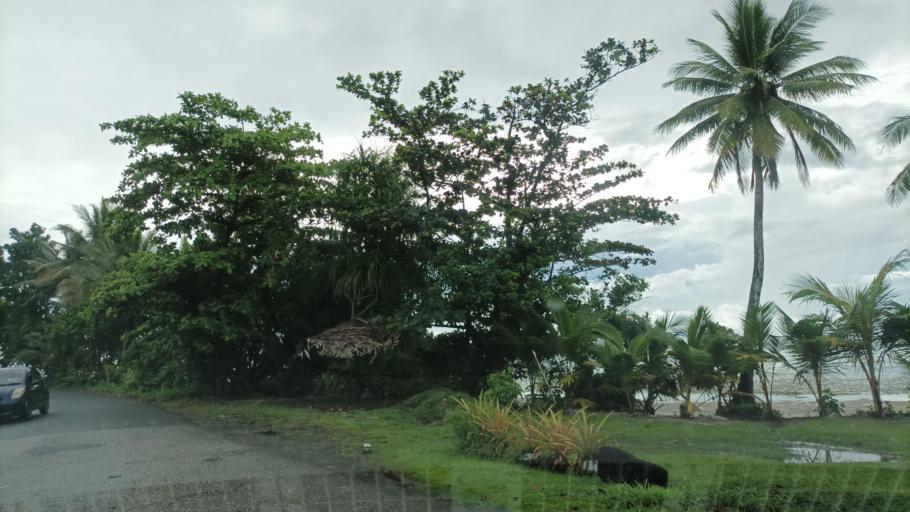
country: FM
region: Kosrae
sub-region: Lelu Municipality
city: Lelu
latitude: 5.3407
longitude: 163.0193
